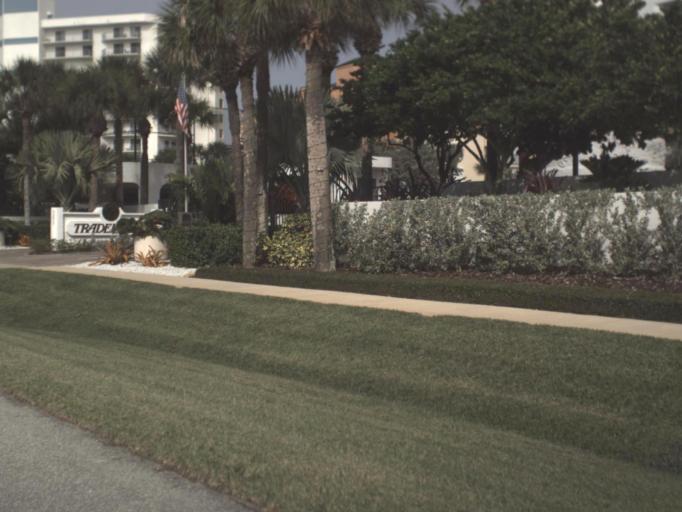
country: US
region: Florida
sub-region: Volusia County
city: Edgewater
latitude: 28.9736
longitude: -80.8559
